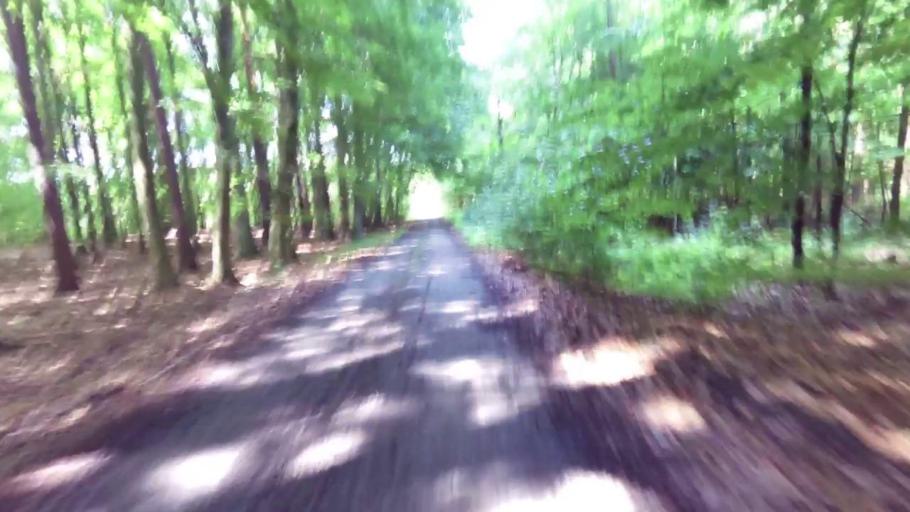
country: PL
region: West Pomeranian Voivodeship
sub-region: Powiat stargardzki
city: Kobylanka
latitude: 53.3481
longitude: 14.8268
